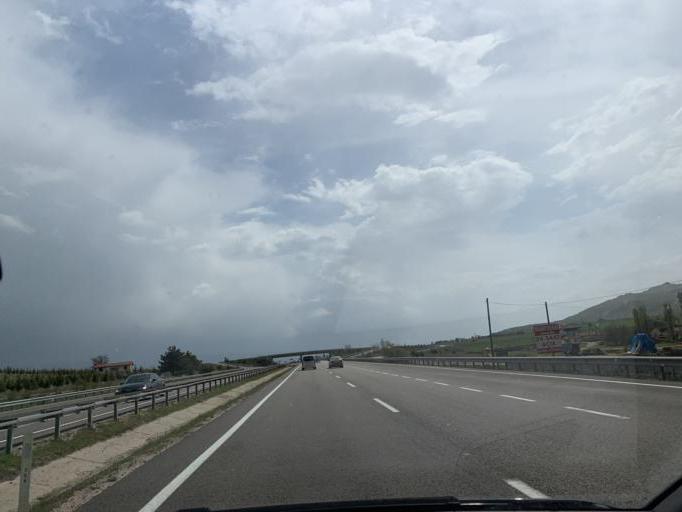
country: TR
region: Eskisehir
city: Sivrihisar
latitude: 39.4567
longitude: 31.5753
